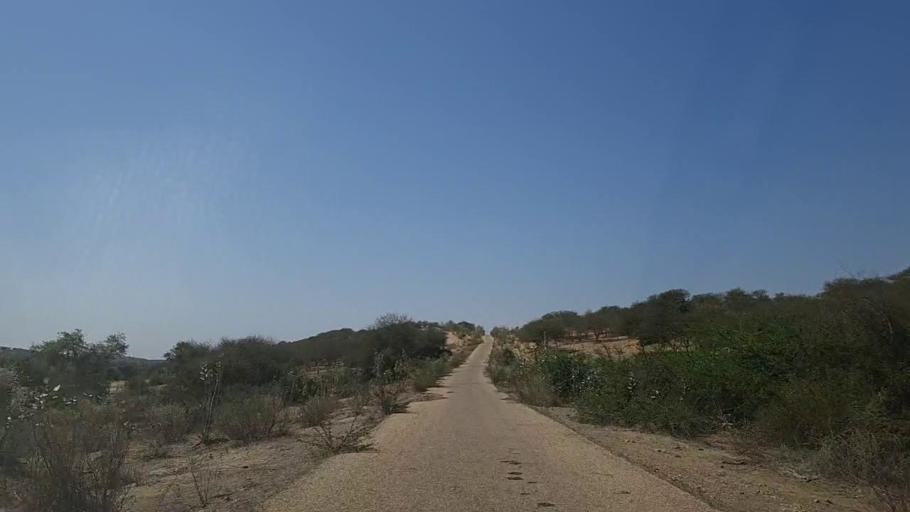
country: PK
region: Sindh
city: Mithi
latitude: 24.8108
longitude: 69.6504
